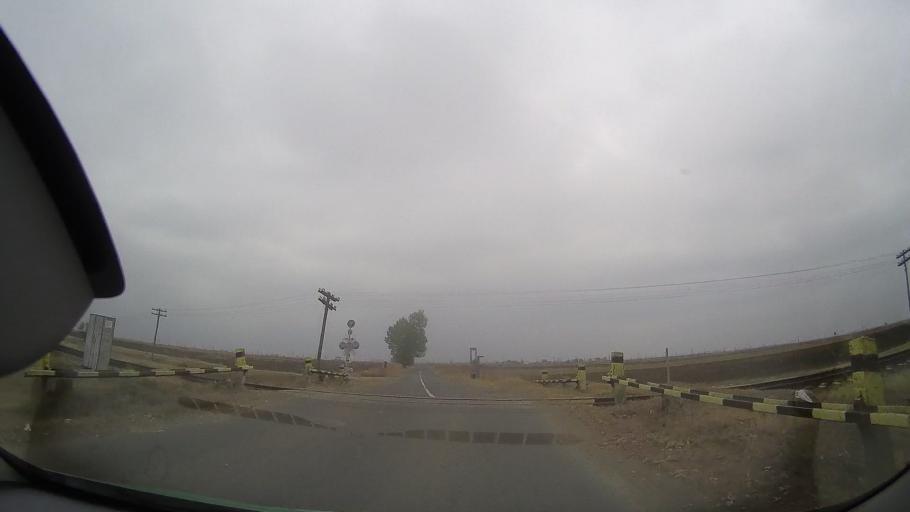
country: RO
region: Buzau
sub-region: Comuna Glodeanu-Silistea
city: Glodeanu-Silistea
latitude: 44.8103
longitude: 26.8557
